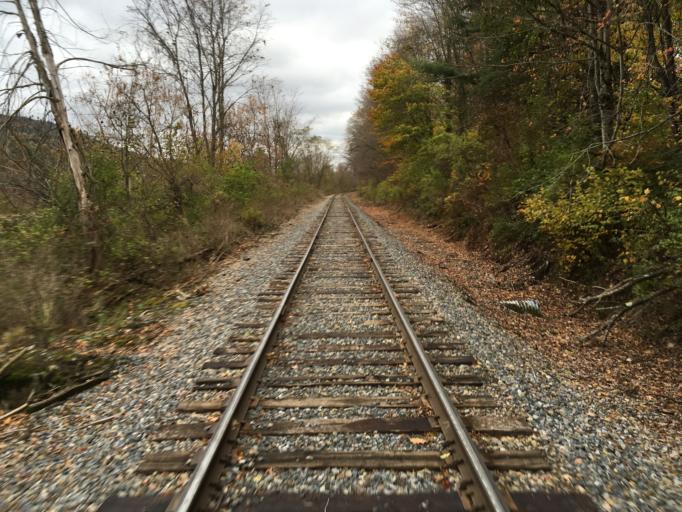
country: US
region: New Hampshire
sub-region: Grafton County
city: Woodsville
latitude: 44.1803
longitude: -72.0590
